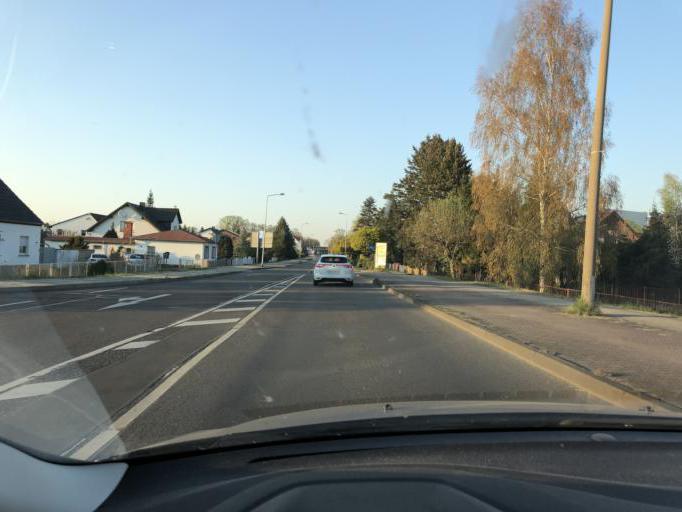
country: DE
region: Brandenburg
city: Spremberg
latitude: 51.5246
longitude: 14.3349
